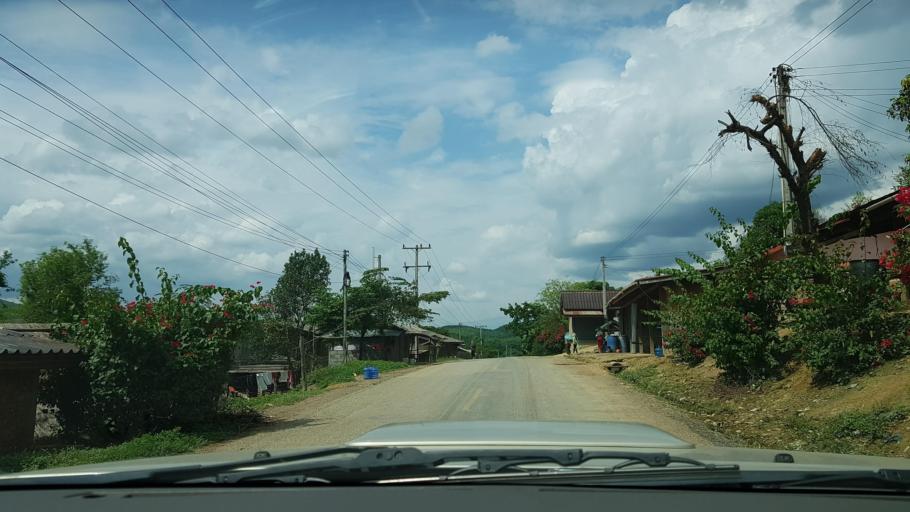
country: LA
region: Loungnamtha
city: Muang Nale
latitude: 20.2355
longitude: 101.5673
